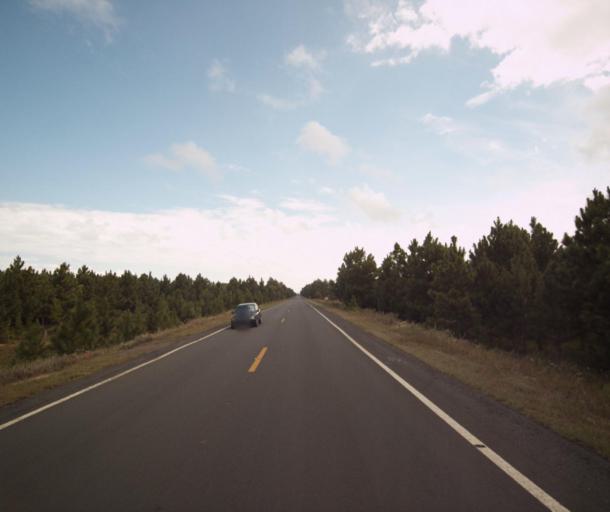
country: BR
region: Rio Grande do Sul
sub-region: Tapes
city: Tapes
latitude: -31.4266
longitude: -51.1849
